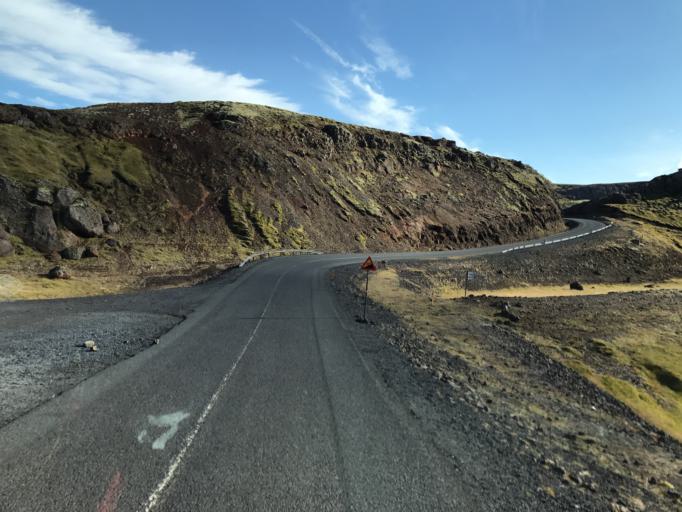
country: IS
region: South
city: Hveragerdi
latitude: 64.1138
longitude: -21.2969
